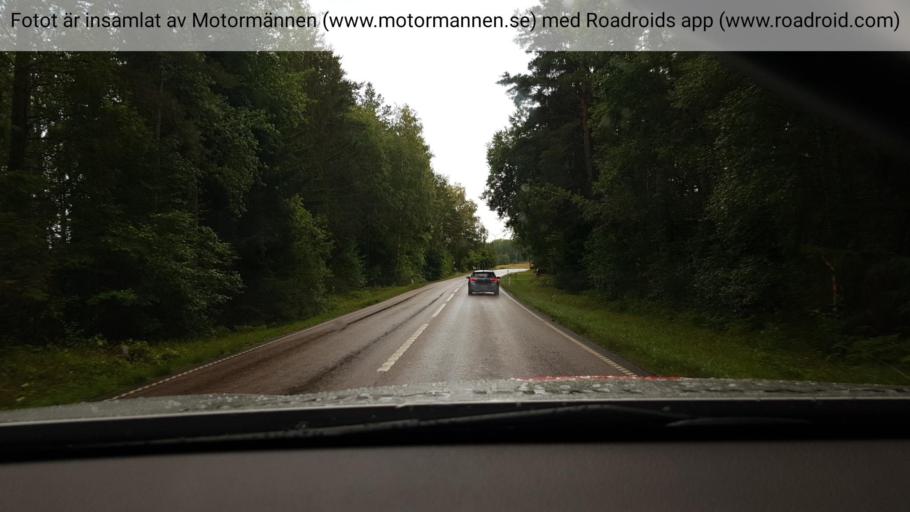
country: SE
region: Stockholm
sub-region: Norrtalje Kommun
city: Norrtalje
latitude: 59.8655
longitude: 18.6940
